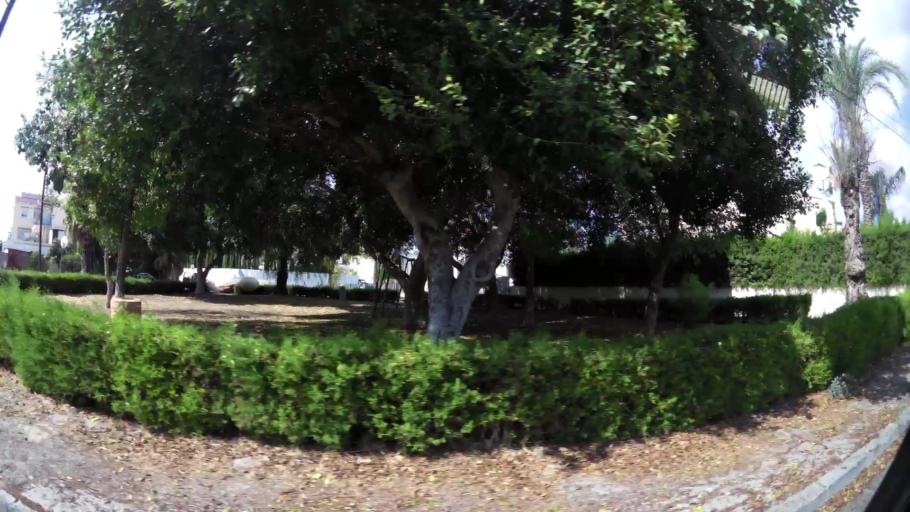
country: CY
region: Larnaka
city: Larnaca
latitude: 34.9174
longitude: 33.6183
